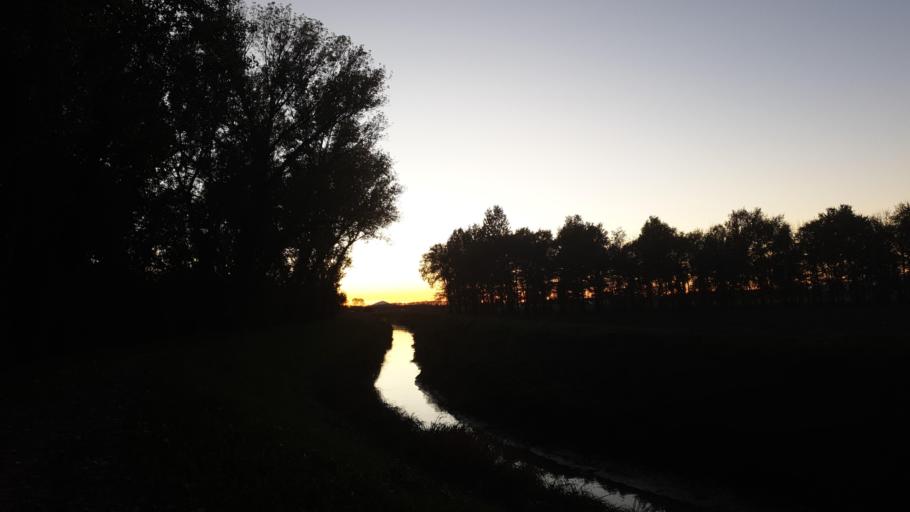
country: IT
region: Veneto
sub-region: Provincia di Venezia
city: Fiesso
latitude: 45.4342
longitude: 12.0381
